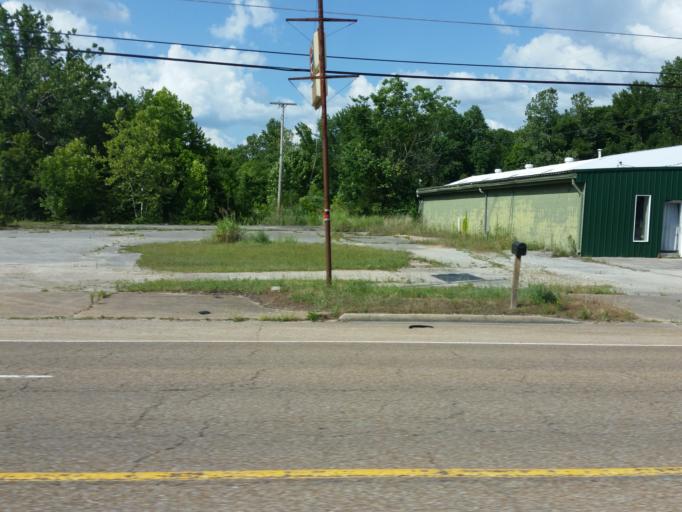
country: US
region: Tennessee
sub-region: Henderson County
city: Lexington
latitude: 35.6428
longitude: -88.3843
